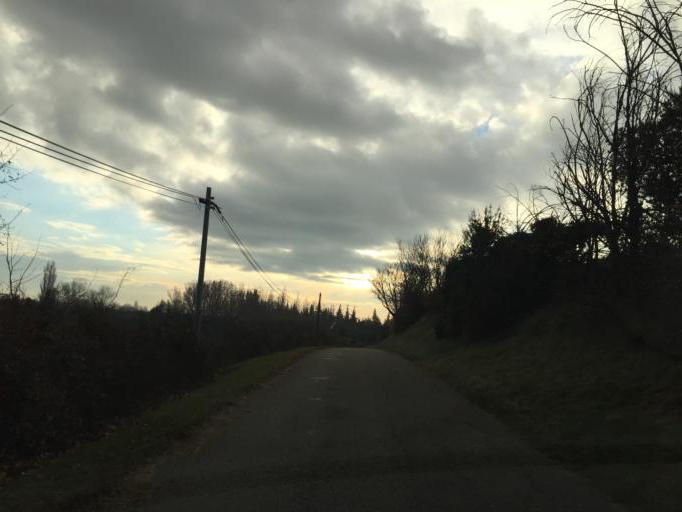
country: FR
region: Provence-Alpes-Cote d'Azur
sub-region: Departement du Vaucluse
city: Courthezon
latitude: 44.1023
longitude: 4.8810
